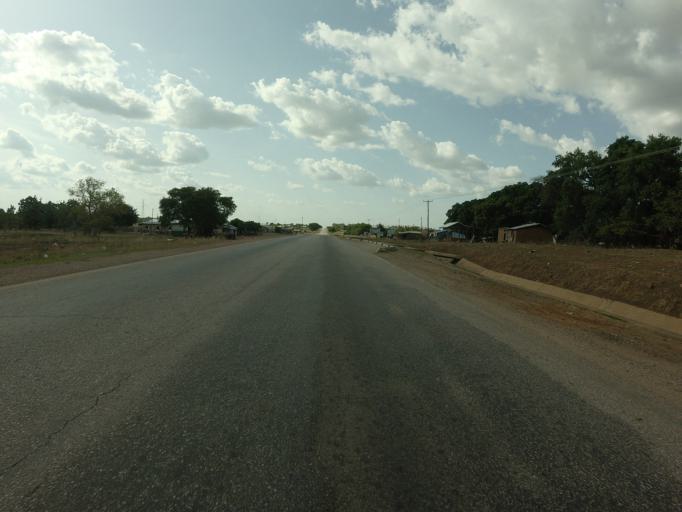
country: GH
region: Upper East
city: Bolgatanga
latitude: 10.6800
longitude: -0.8621
